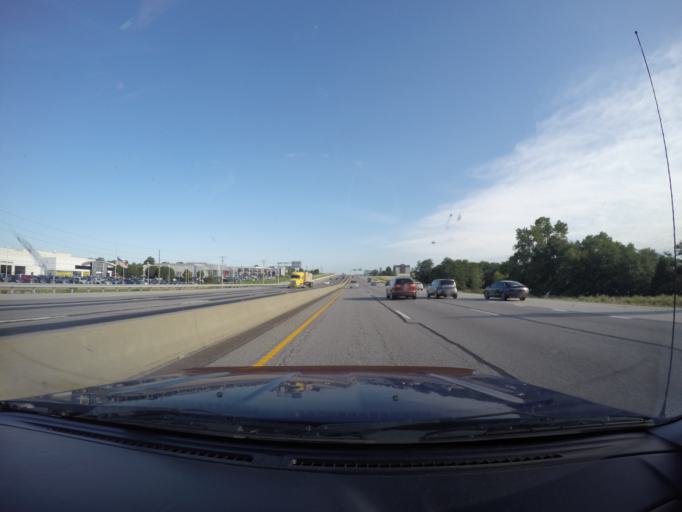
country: US
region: Missouri
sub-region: Platte County
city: Weatherby Lake
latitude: 39.2661
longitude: -94.6641
